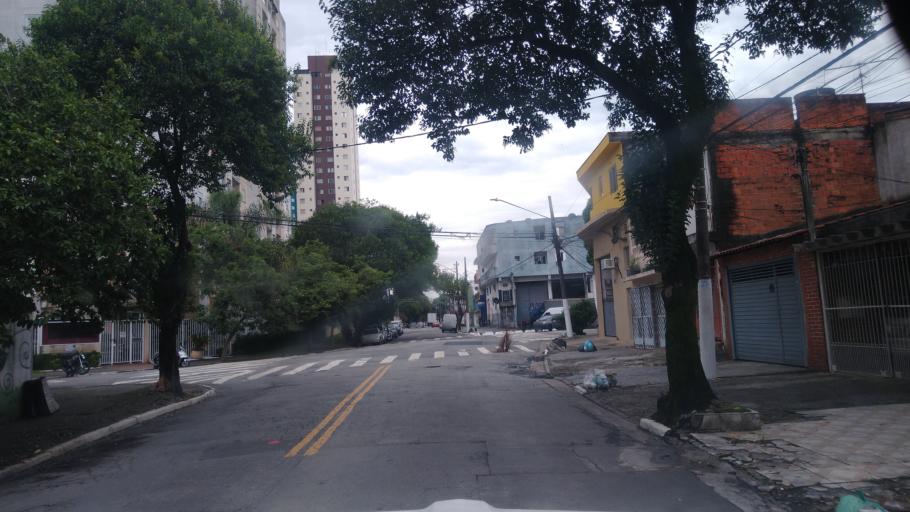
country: BR
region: Sao Paulo
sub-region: Guarulhos
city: Guarulhos
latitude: -23.5202
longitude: -46.5656
